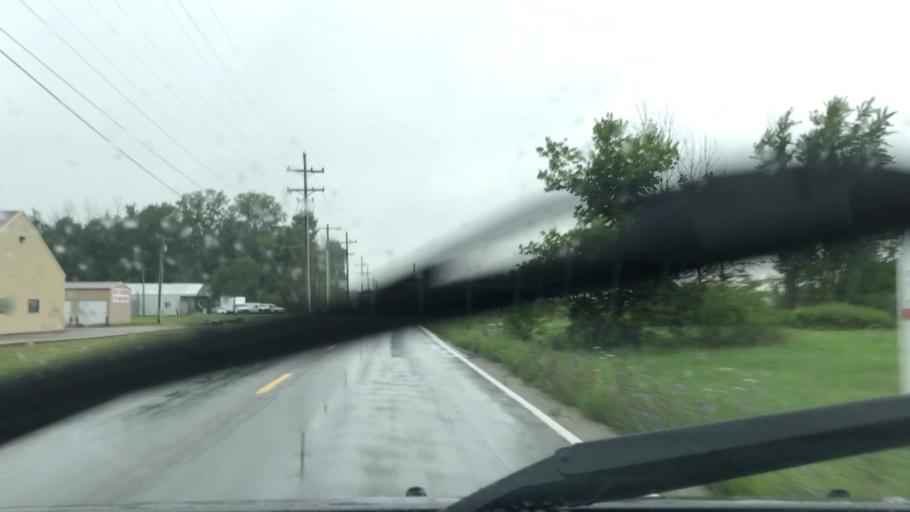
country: US
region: Indiana
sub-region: Hamilton County
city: Sheridan
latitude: 40.1298
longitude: -86.2311
